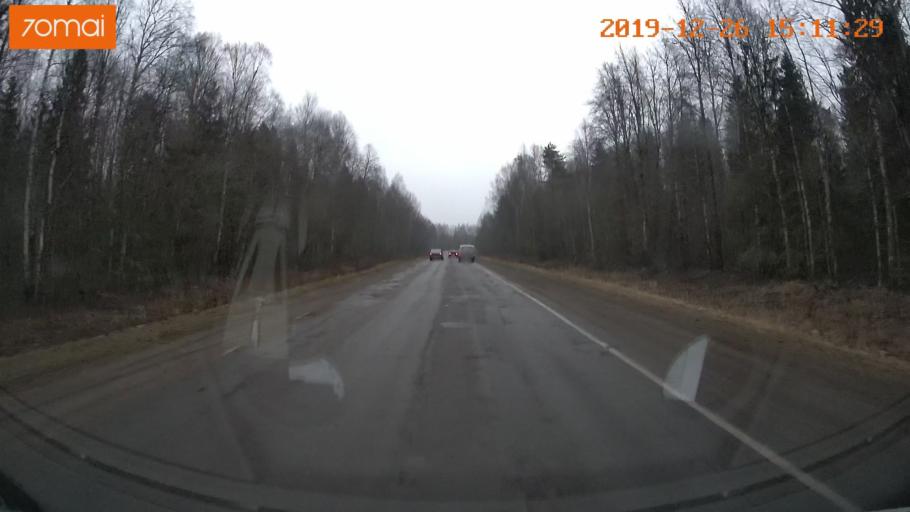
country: RU
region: Jaroslavl
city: Rybinsk
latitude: 58.1343
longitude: 38.8623
